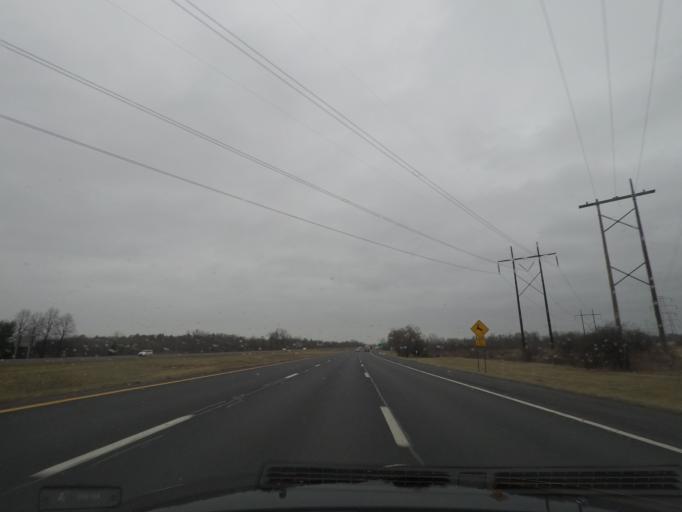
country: US
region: New York
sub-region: Rensselaer County
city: Hampton Manor
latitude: 42.6357
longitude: -73.7070
